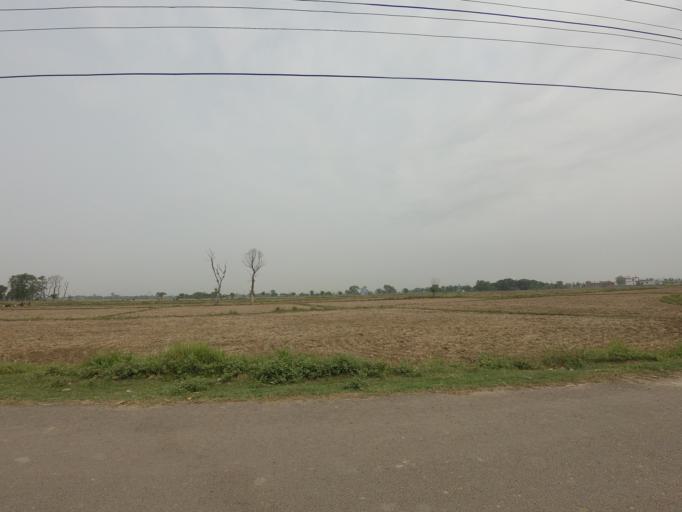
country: NP
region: Western Region
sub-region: Lumbini Zone
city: Bhairahawa
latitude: 27.4890
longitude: 83.4282
